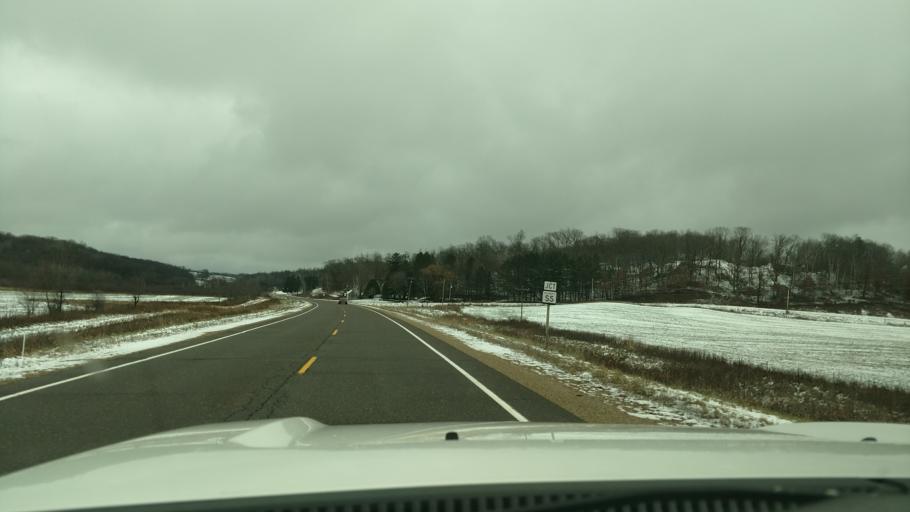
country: US
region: Wisconsin
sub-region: Dunn County
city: Tainter Lake
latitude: 45.1265
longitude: -91.8496
